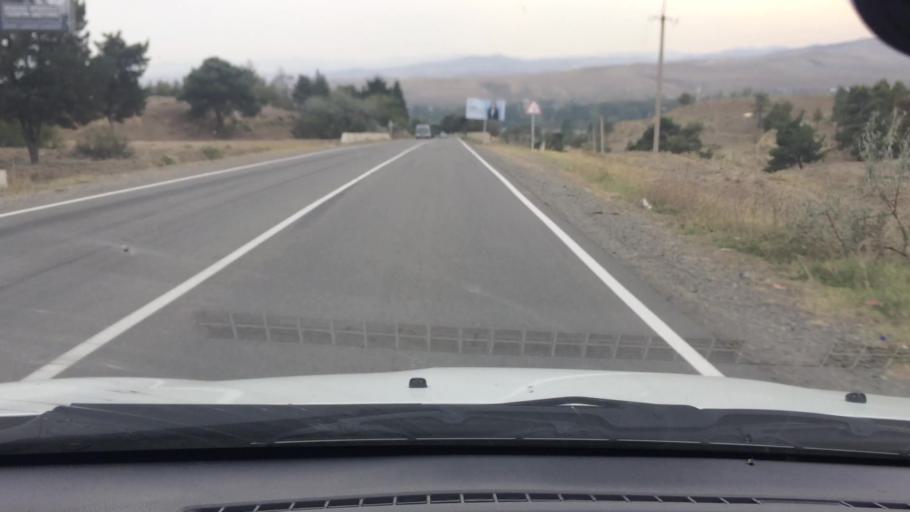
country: GE
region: Kvemo Kartli
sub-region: Gardabani
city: Gardabani
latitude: 41.3470
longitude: 45.0685
